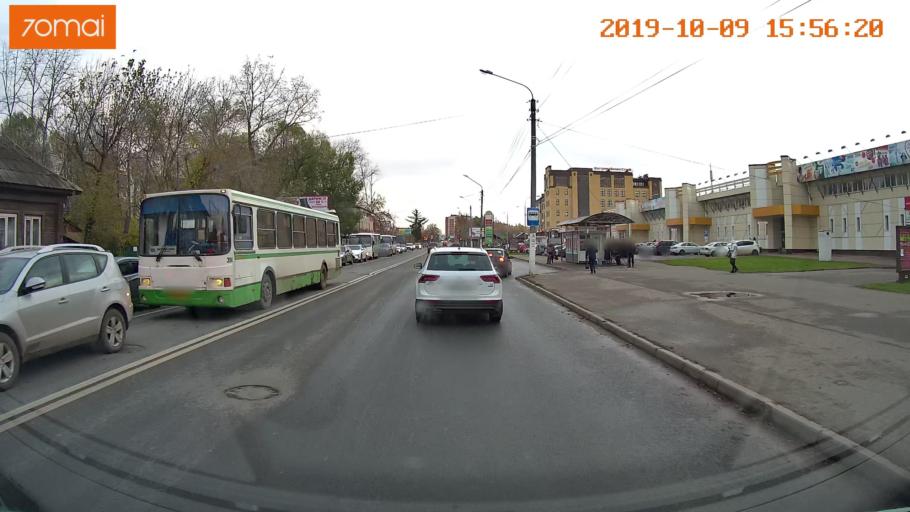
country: RU
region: Kostroma
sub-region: Kostromskoy Rayon
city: Kostroma
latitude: 57.7751
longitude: 40.9448
